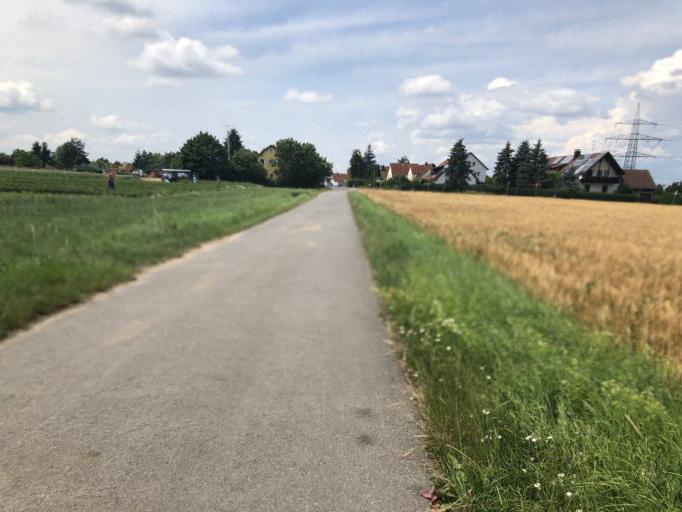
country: DE
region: Bavaria
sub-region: Regierungsbezirk Mittelfranken
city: Erlangen
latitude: 49.5788
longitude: 10.9495
